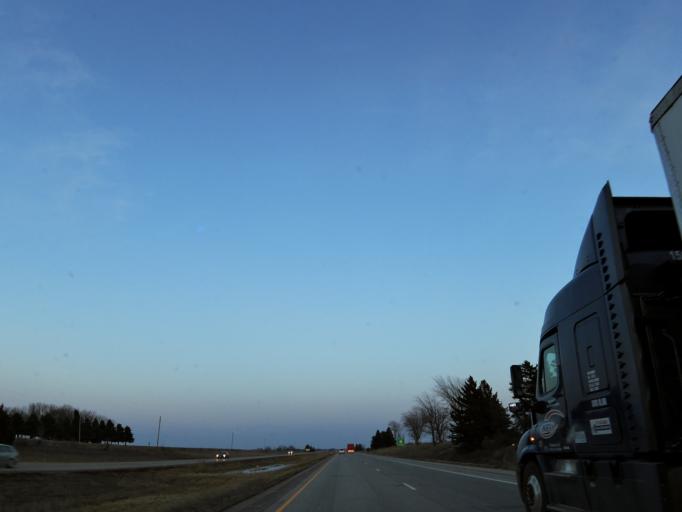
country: US
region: Minnesota
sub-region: Mower County
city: Austin
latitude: 43.6736
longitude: -92.8191
